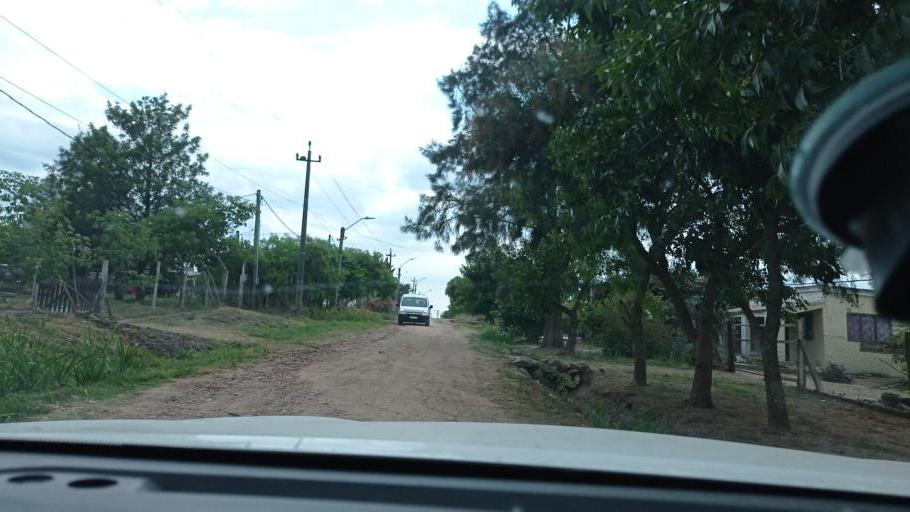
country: UY
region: Canelones
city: Pando
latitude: -34.7067
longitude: -55.9694
